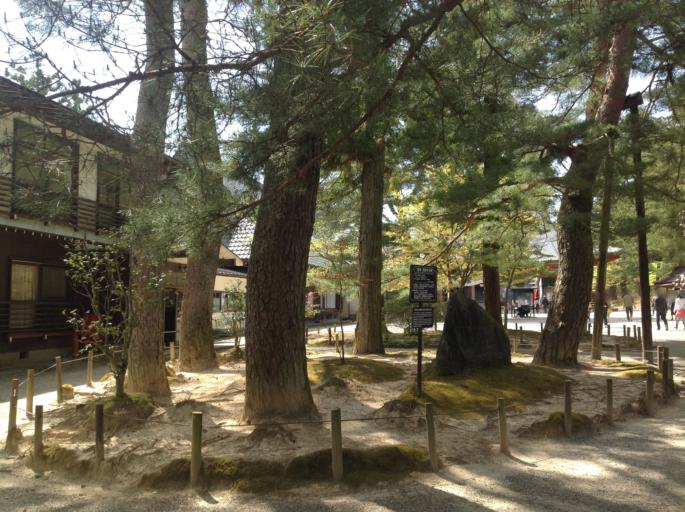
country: JP
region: Iwate
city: Ichinoseki
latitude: 38.9870
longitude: 141.1085
